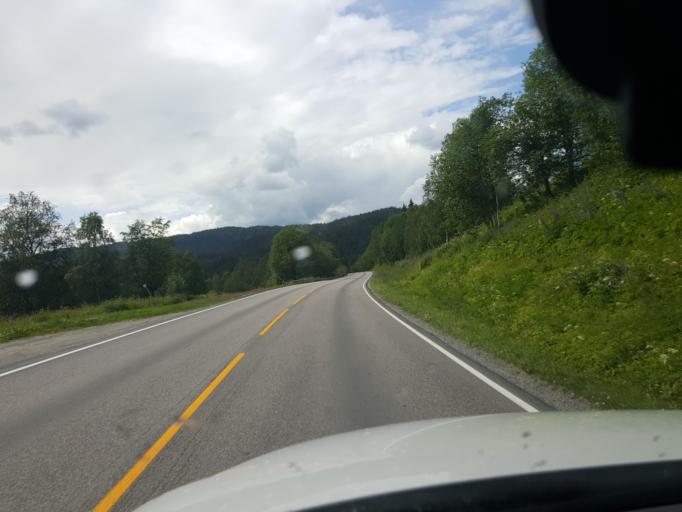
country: NO
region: Nordland
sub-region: Rana
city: Mo i Rana
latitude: 66.4057
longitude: 14.4847
